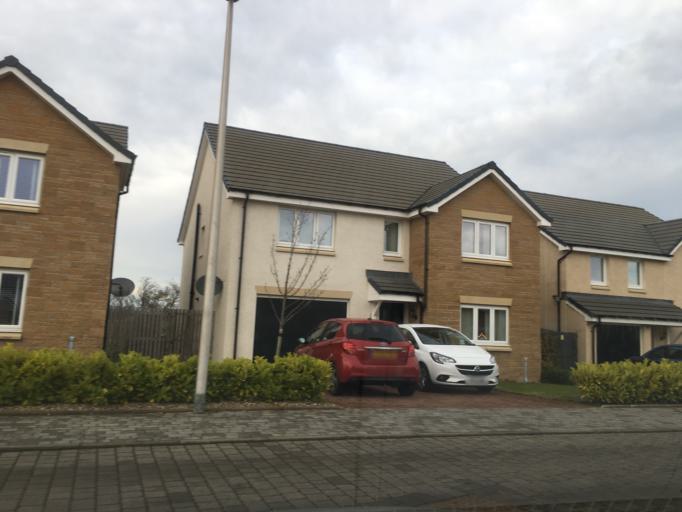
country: GB
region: Scotland
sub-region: Midlothian
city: Loanhead
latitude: 55.8731
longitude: -3.1806
